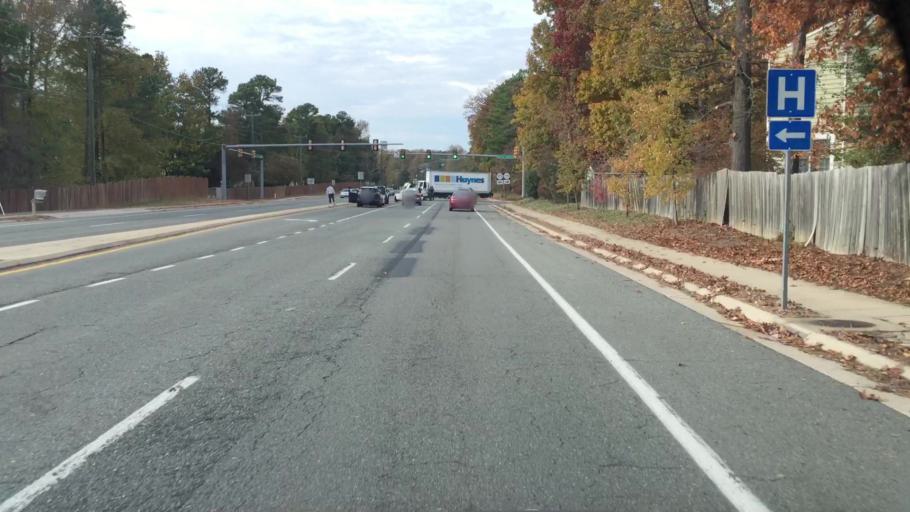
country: US
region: Virginia
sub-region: Chesterfield County
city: Bon Air
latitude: 37.5135
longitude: -77.5898
